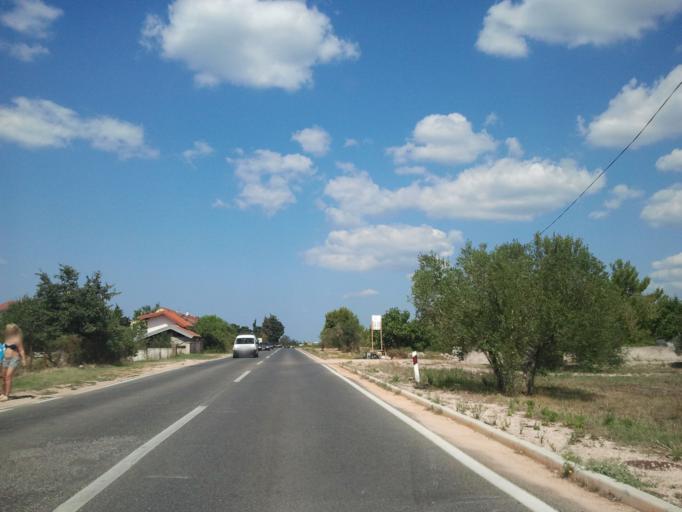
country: HR
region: Zadarska
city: Turanj
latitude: 43.9763
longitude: 15.3980
